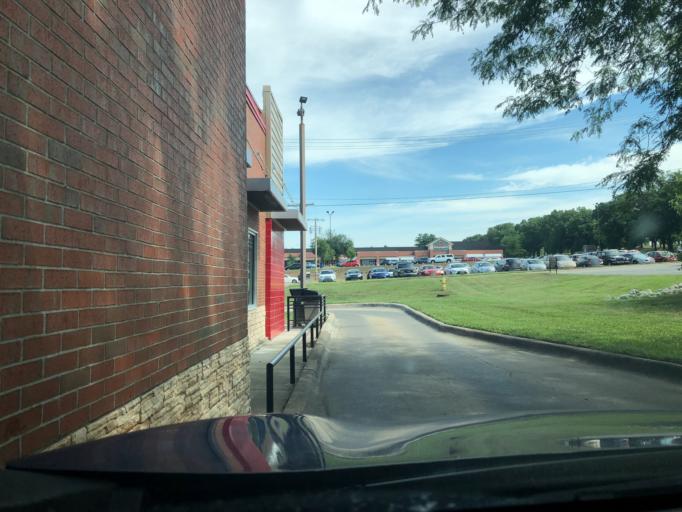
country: US
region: Kansas
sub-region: Leavenworth County
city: Leavenworth
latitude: 39.3378
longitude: -94.9230
